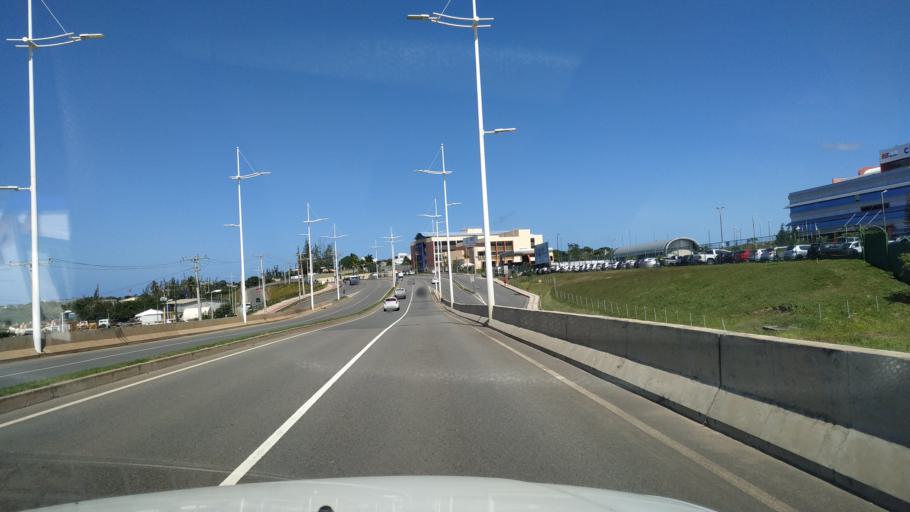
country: BR
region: Bahia
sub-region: Lauro De Freitas
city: Lauro de Freitas
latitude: -12.9377
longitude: -38.3859
